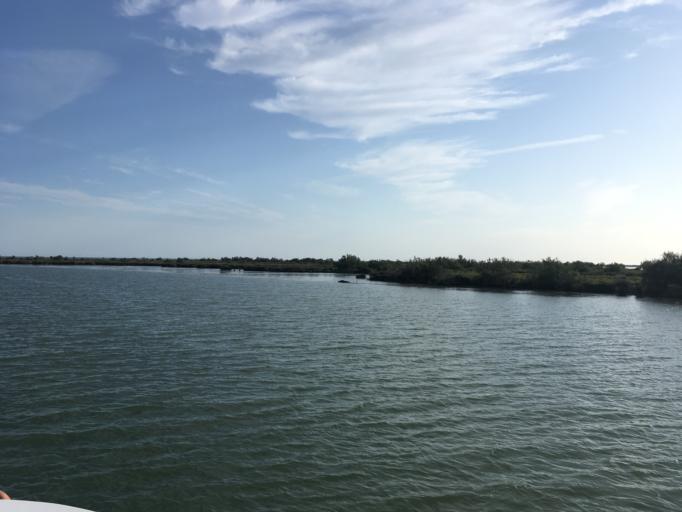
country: FR
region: Provence-Alpes-Cote d'Azur
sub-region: Departement des Bouches-du-Rhone
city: Saintes-Maries-de-la-Mer
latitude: 43.4600
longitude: 4.3897
